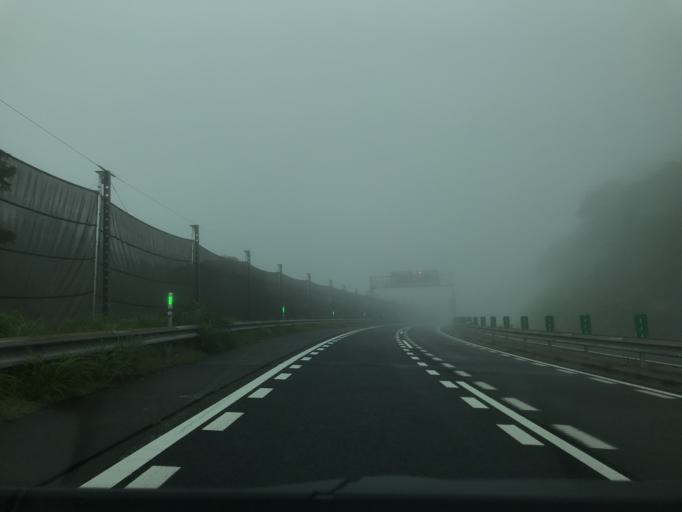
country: JP
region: Oita
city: Hiji
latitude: 33.3593
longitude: 131.4501
